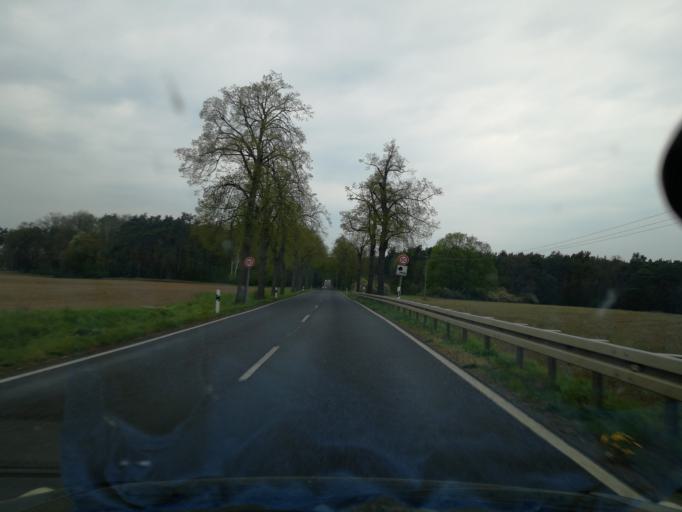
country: DE
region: Brandenburg
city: Calau
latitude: 51.7518
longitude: 13.9365
